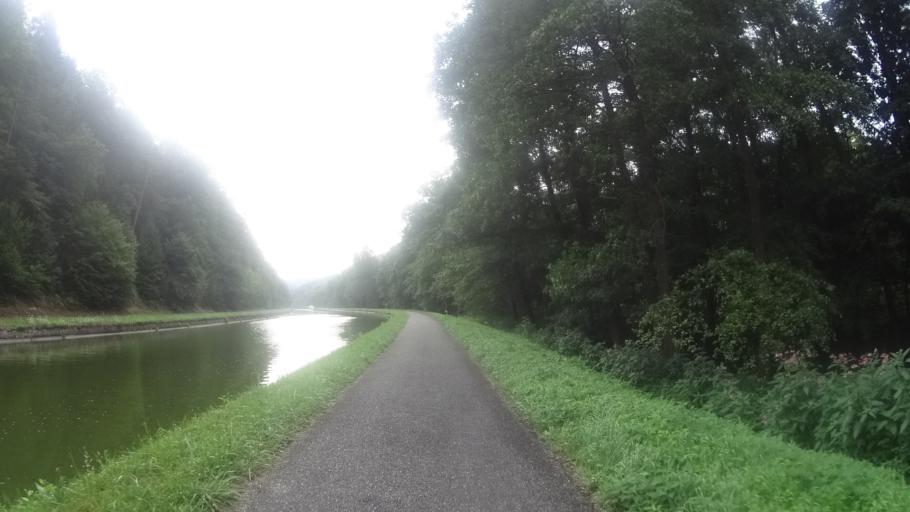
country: FR
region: Lorraine
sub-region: Departement de la Moselle
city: Phalsbourg
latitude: 48.7358
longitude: 7.2752
